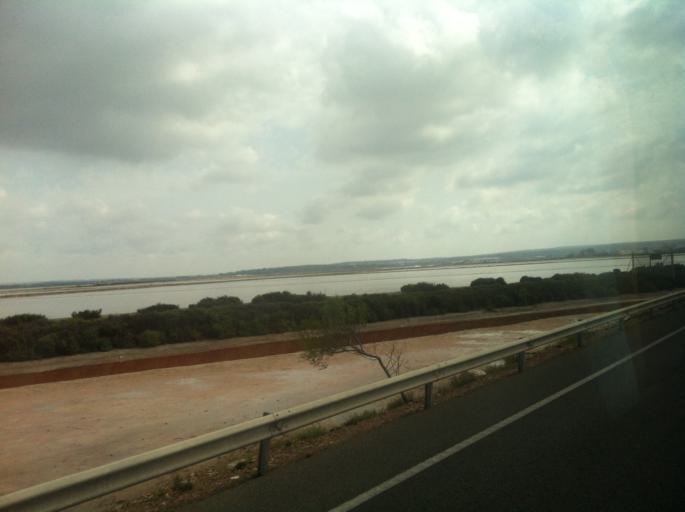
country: ES
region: Valencia
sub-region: Provincia de Alicante
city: Santa Pola
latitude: 38.1849
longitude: -0.6121
